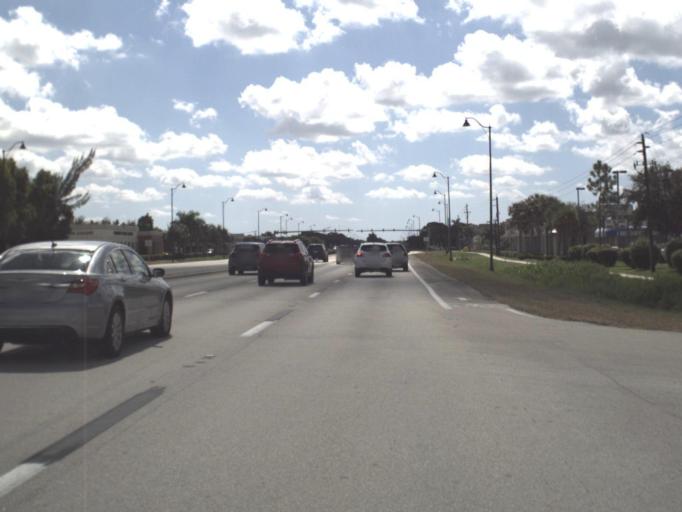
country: US
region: Florida
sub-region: Lee County
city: Bonita Springs
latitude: 26.3211
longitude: -81.8054
